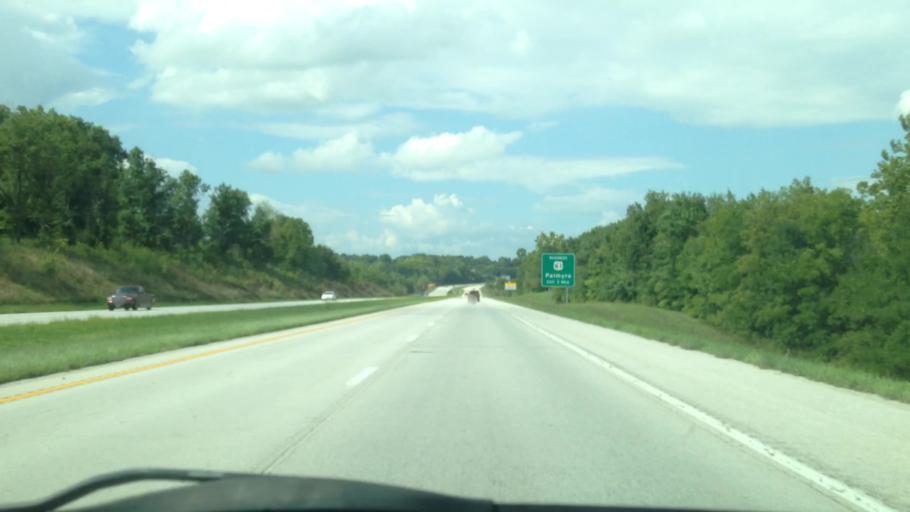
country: US
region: Missouri
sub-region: Marion County
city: Palmyra
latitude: 39.7522
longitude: -91.5179
